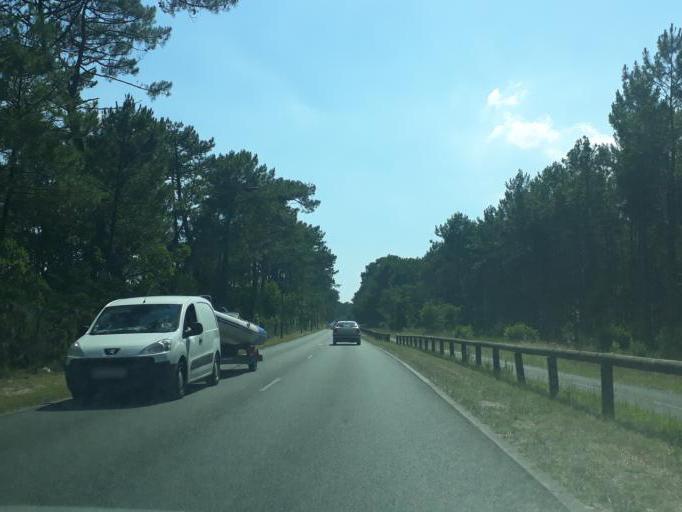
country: FR
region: Aquitaine
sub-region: Departement de la Gironde
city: Ares
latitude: 44.7406
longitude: -1.1881
